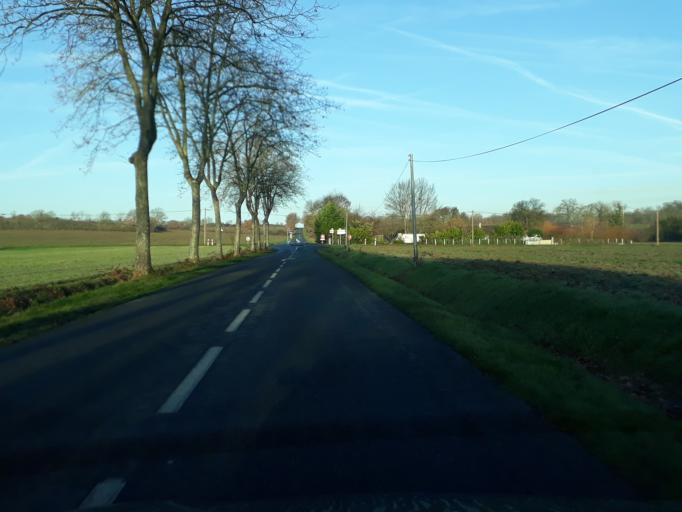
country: FR
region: Midi-Pyrenees
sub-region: Departement de la Haute-Garonne
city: Rieumes
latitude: 43.4278
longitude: 1.1331
